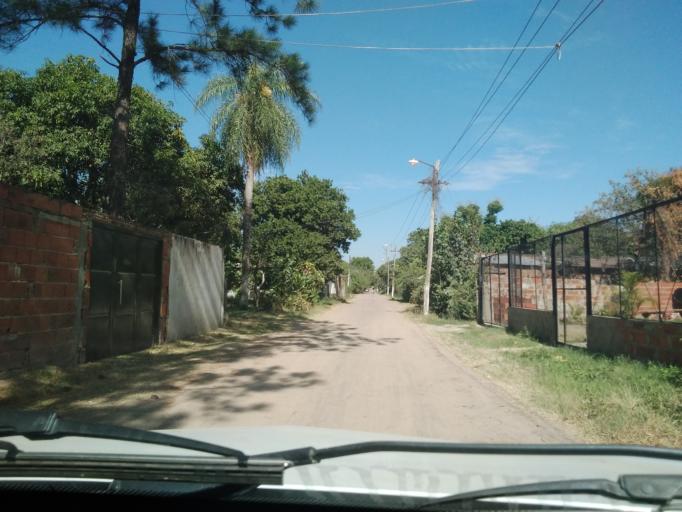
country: AR
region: Corrientes
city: Corrientes
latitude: -27.5134
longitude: -58.8021
